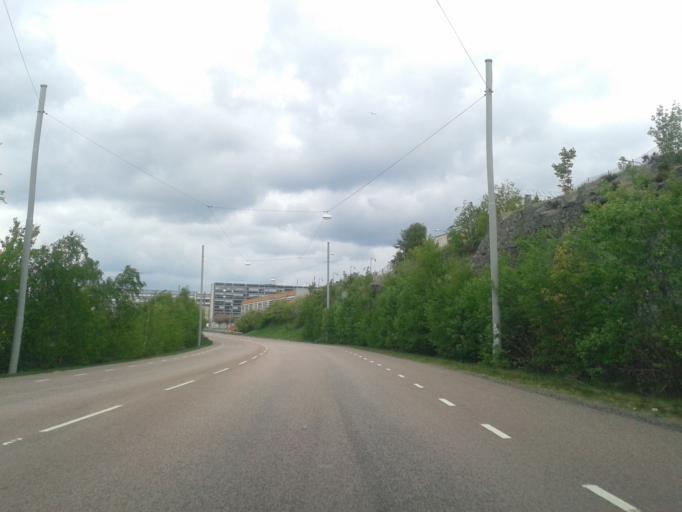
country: SE
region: Vaestra Goetaland
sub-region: Goteborg
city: Gardsten
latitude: 57.8013
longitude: 12.0245
